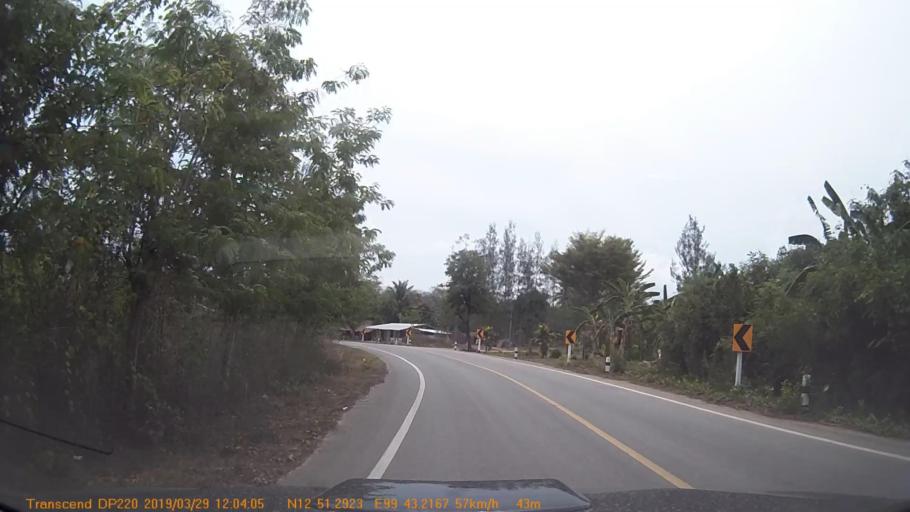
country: TH
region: Phetchaburi
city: Kaeng Krachan
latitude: 12.8547
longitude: 99.7204
